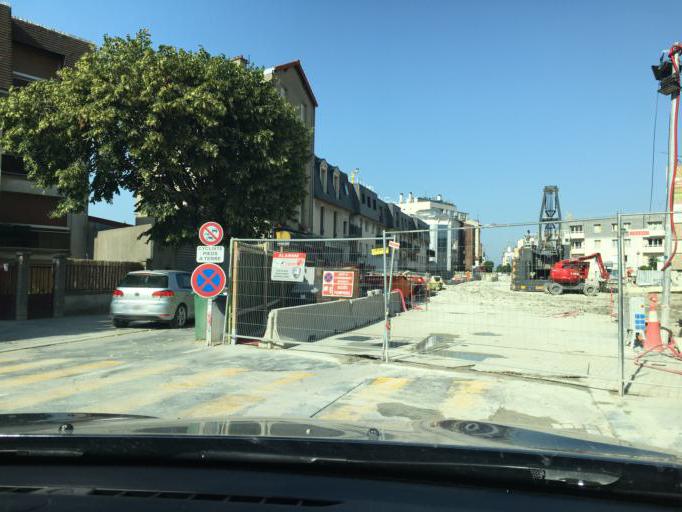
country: FR
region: Ile-de-France
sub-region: Departement de Seine-Saint-Denis
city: Les Lilas
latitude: 48.8811
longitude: 2.4262
